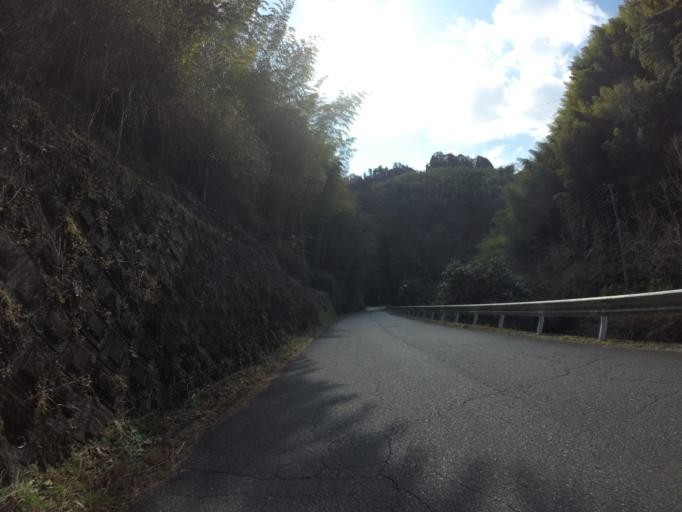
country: JP
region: Shizuoka
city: Shizuoka-shi
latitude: 35.0777
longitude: 138.4771
